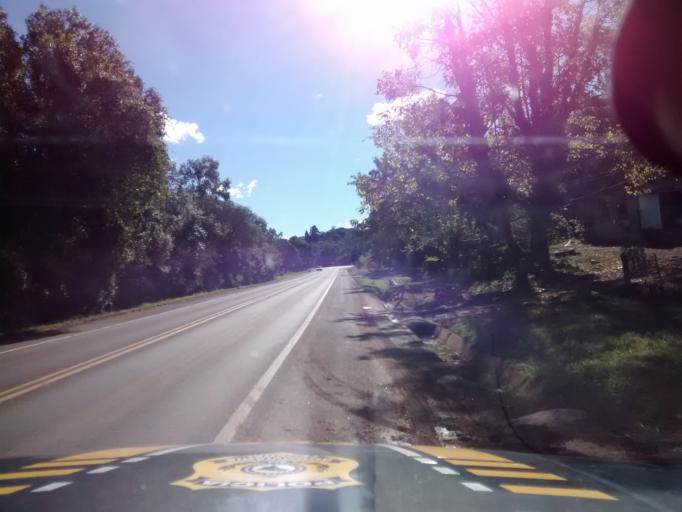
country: BR
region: Rio Grande do Sul
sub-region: Vacaria
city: Vacaria
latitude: -28.3308
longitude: -51.1789
